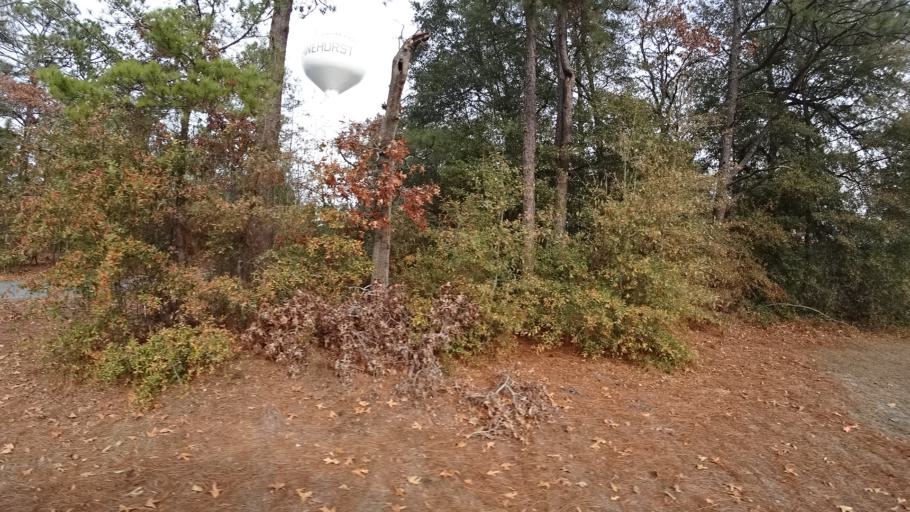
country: US
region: North Carolina
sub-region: Moore County
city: Pinehurst
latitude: 35.2042
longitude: -79.4624
